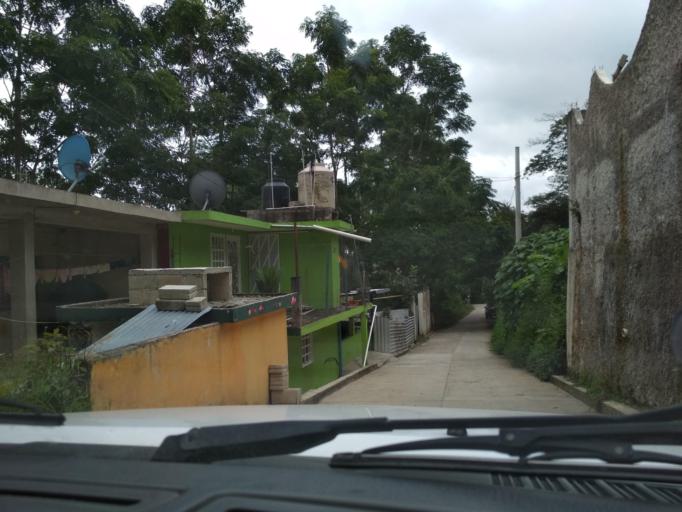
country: MX
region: Veracruz
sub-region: Naolinco
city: El Espinal
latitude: 19.5902
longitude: -96.8797
